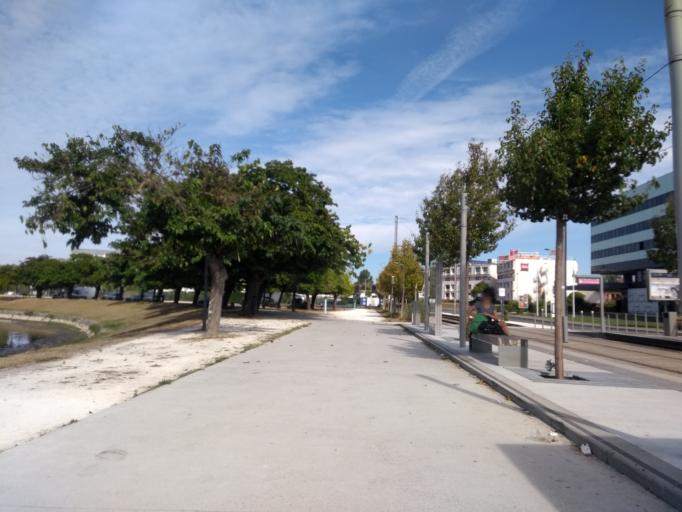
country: FR
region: Aquitaine
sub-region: Departement de la Gironde
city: Le Bouscat
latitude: 44.8894
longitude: -0.5672
